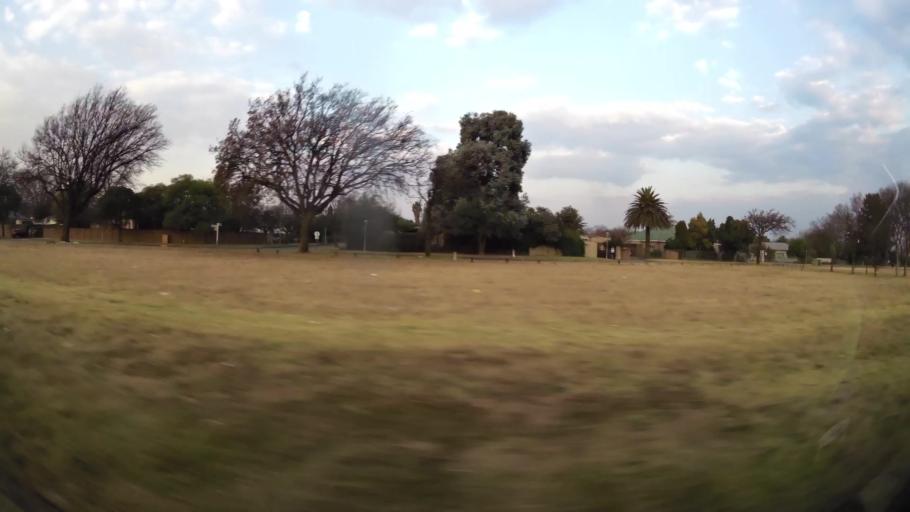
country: ZA
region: Gauteng
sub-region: Ekurhuleni Metropolitan Municipality
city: Benoni
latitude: -26.1731
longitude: 28.3106
